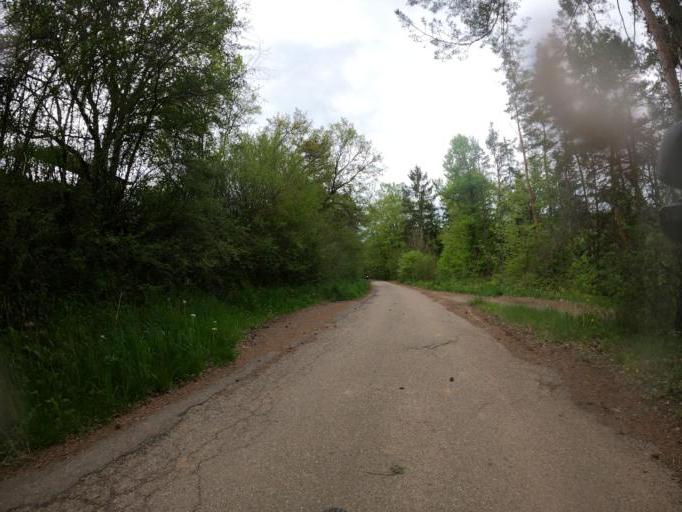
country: DE
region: Baden-Wuerttemberg
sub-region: Karlsruhe Region
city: Nagold
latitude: 48.5219
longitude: 8.6959
